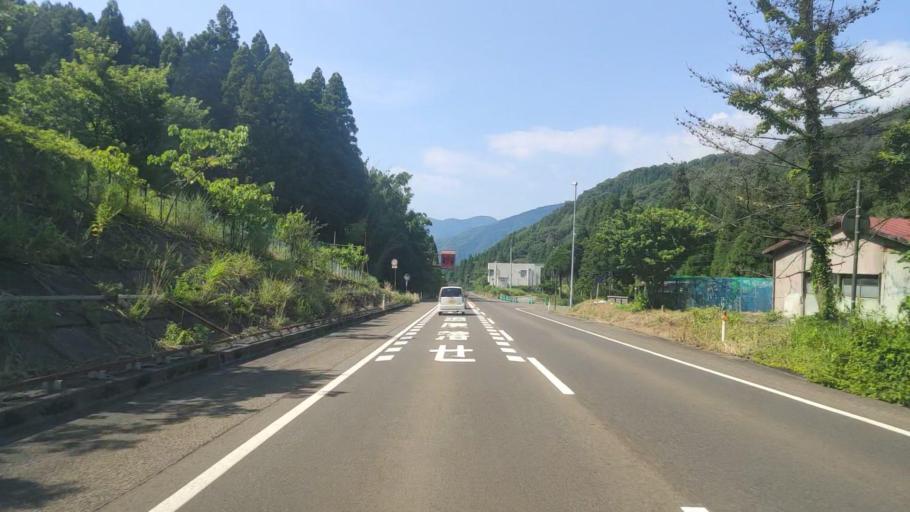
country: JP
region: Fukui
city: Tsuruga
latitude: 35.5879
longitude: 136.1242
